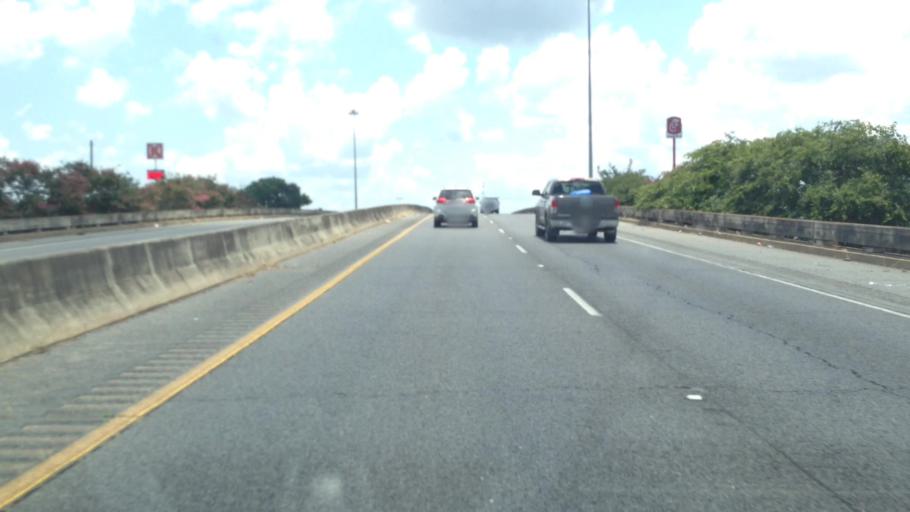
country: US
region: Louisiana
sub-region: Rapides Parish
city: Alexandria
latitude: 31.2876
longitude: -92.4754
